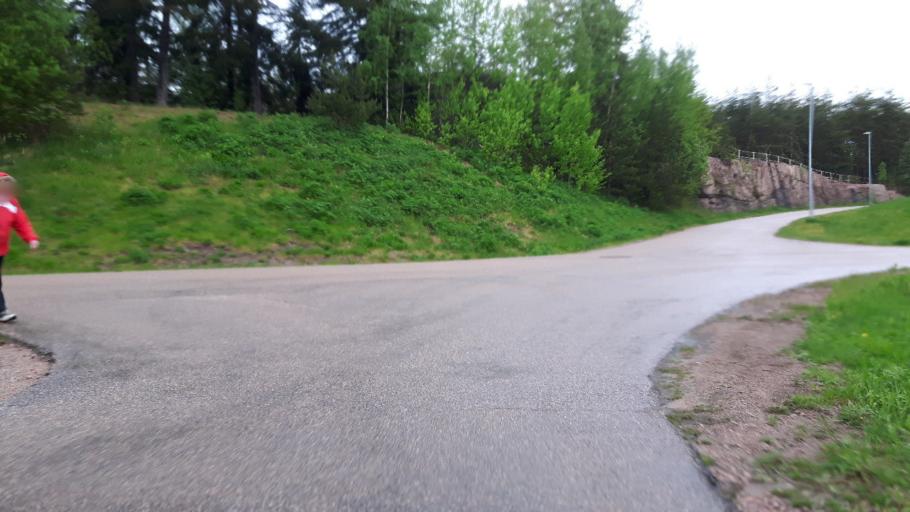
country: FI
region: Kymenlaakso
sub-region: Kotka-Hamina
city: Karhula
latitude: 60.5333
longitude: 26.9555
